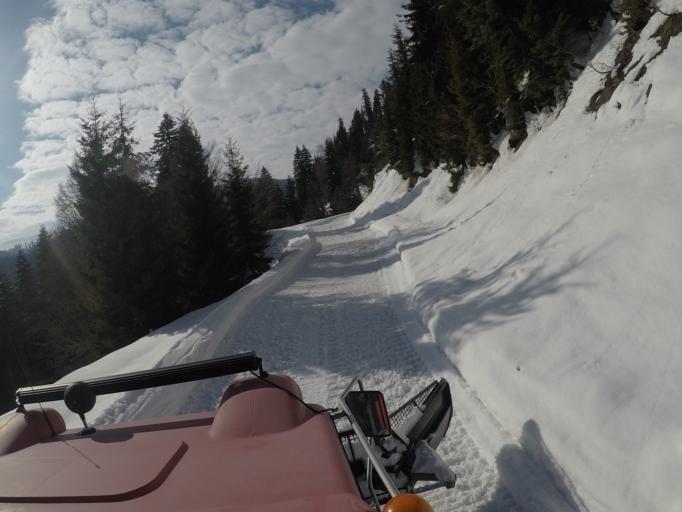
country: GE
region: Samtskhe-Javakheti
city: Adigeni
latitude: 41.6365
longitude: 42.5796
